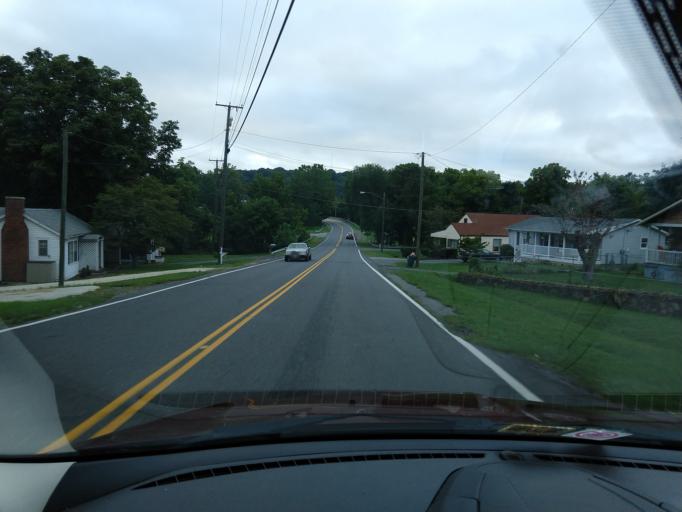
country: US
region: Virginia
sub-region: City of Covington
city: Fairlawn
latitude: 37.7543
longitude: -79.9873
